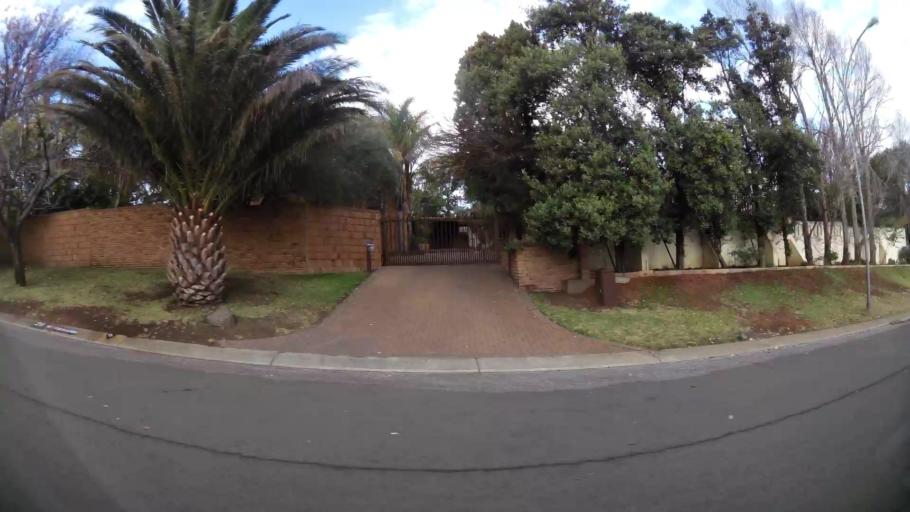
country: ZA
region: Orange Free State
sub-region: Mangaung Metropolitan Municipality
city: Bloemfontein
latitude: -29.0863
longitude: 26.1987
